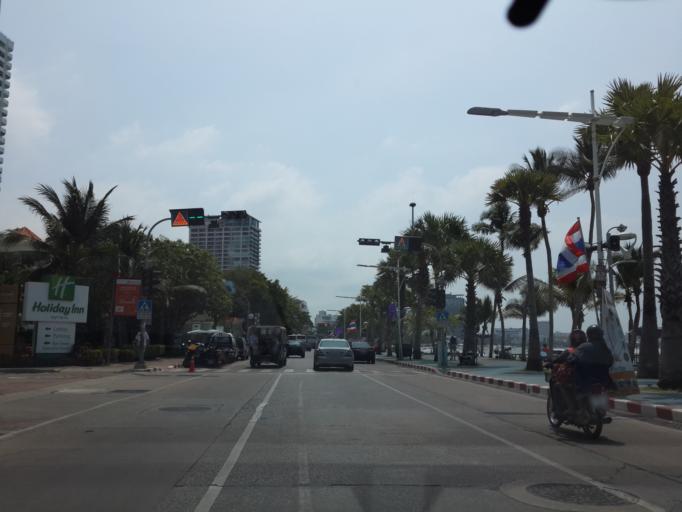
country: TH
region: Chon Buri
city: Phatthaya
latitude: 12.9479
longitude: 100.8846
